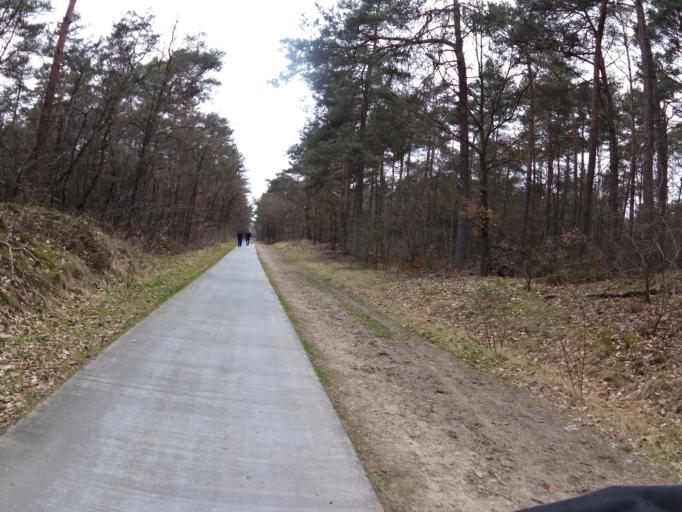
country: NL
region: Drenthe
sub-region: Gemeente Westerveld
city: Dwingeloo
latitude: 52.9466
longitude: 6.3235
